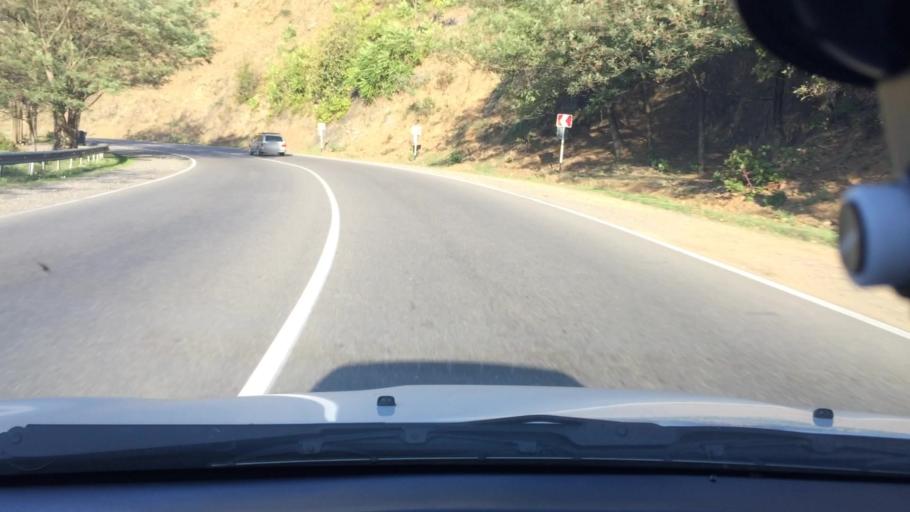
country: GE
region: Imereti
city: Kharagauli
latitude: 42.1146
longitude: 43.2859
